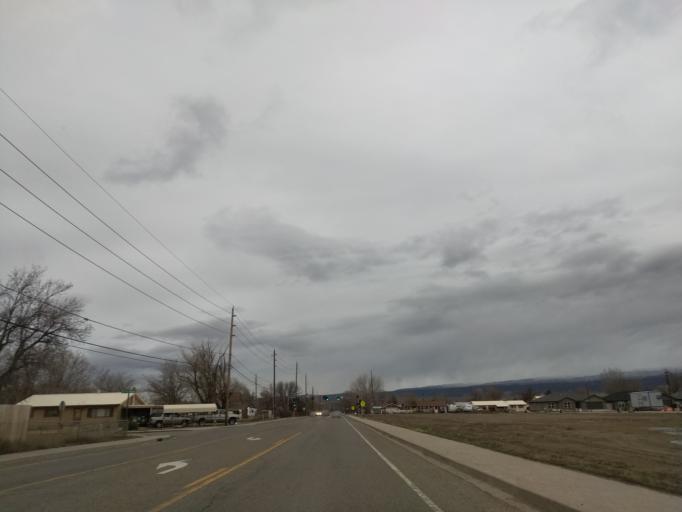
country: US
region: Colorado
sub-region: Mesa County
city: Fruitvale
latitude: 39.0719
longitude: -108.4966
